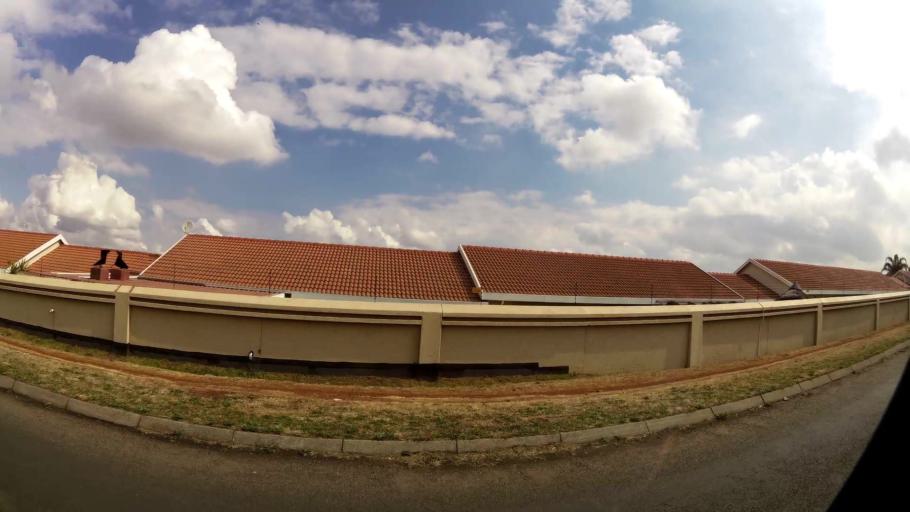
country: ZA
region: Gauteng
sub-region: Sedibeng District Municipality
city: Vanderbijlpark
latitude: -26.7399
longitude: 27.8442
